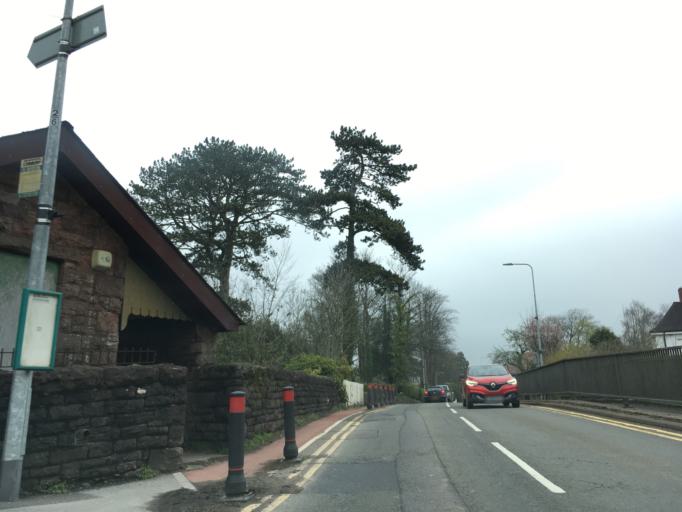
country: GB
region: Wales
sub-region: Cardiff
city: Cardiff
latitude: 51.5322
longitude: -3.1821
